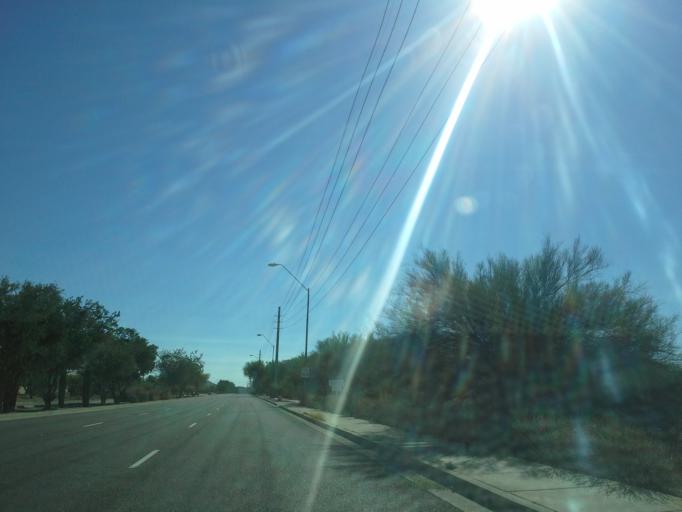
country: US
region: Arizona
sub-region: Maricopa County
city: Scottsdale
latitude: 33.5824
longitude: -111.8295
